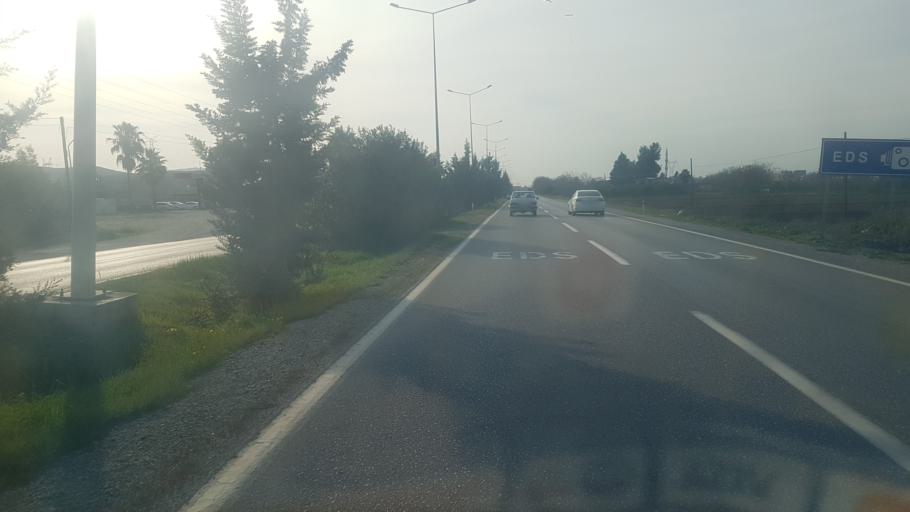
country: TR
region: Osmaniye
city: Toprakkale
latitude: 37.0549
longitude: 36.1329
